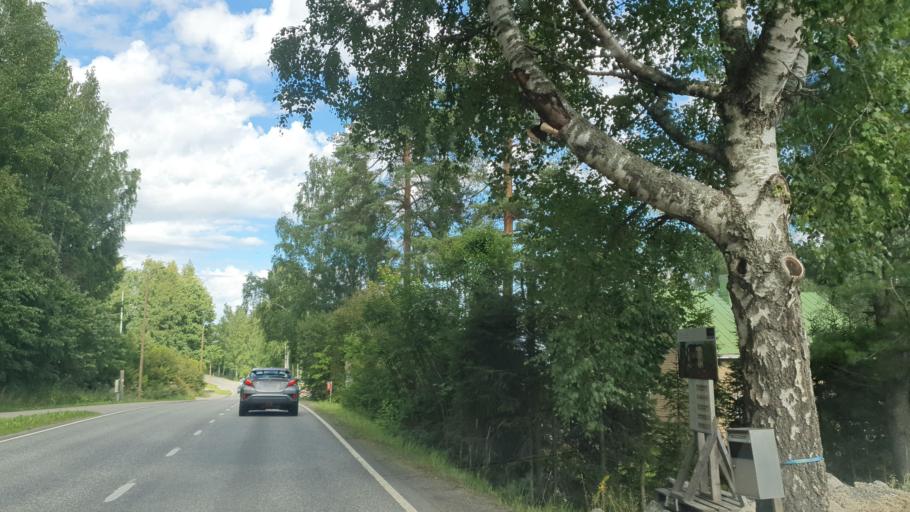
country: FI
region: Central Finland
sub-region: Jyvaeskylae
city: Saeynaetsalo
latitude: 62.1454
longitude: 25.7479
